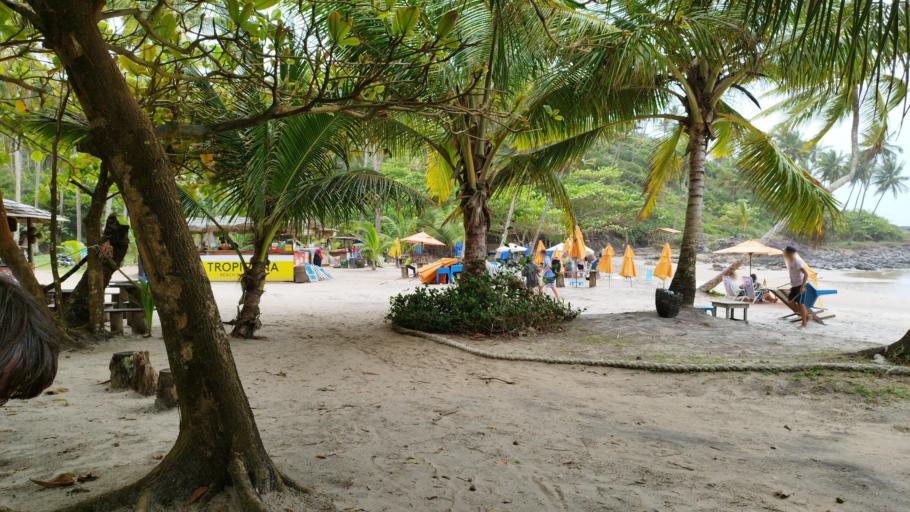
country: BR
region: Bahia
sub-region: Itacare
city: Itacare
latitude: -14.2843
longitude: -38.9853
